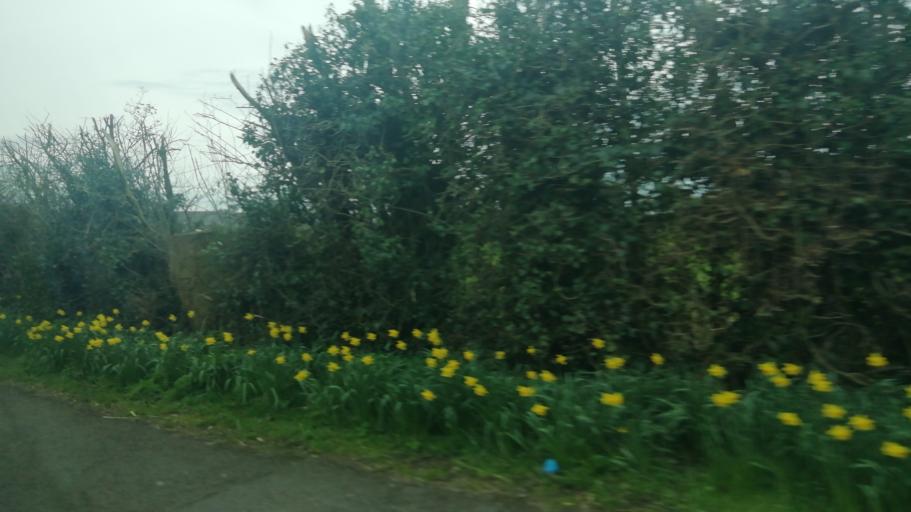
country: IE
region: Leinster
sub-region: Kildare
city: Derrinturn
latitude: 53.3346
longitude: -6.9317
